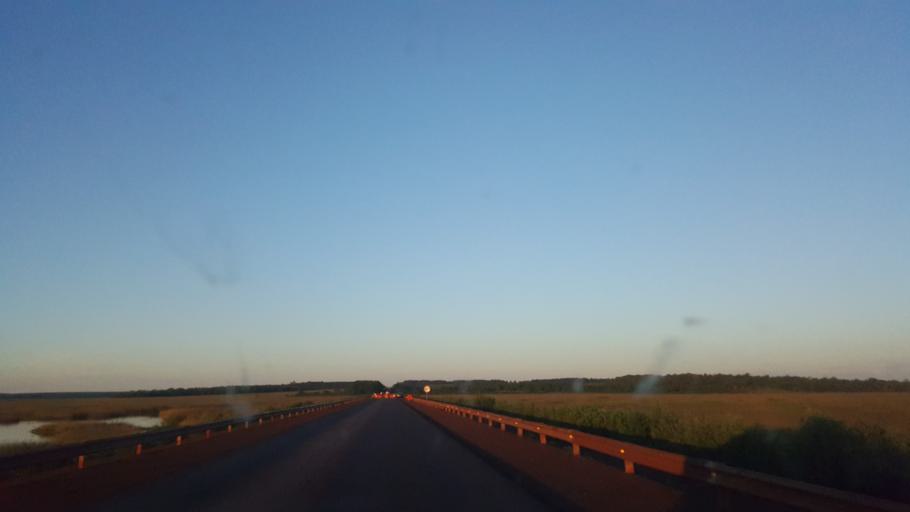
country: AR
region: Corrientes
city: Santo Tome
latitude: -28.3849
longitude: -55.9633
